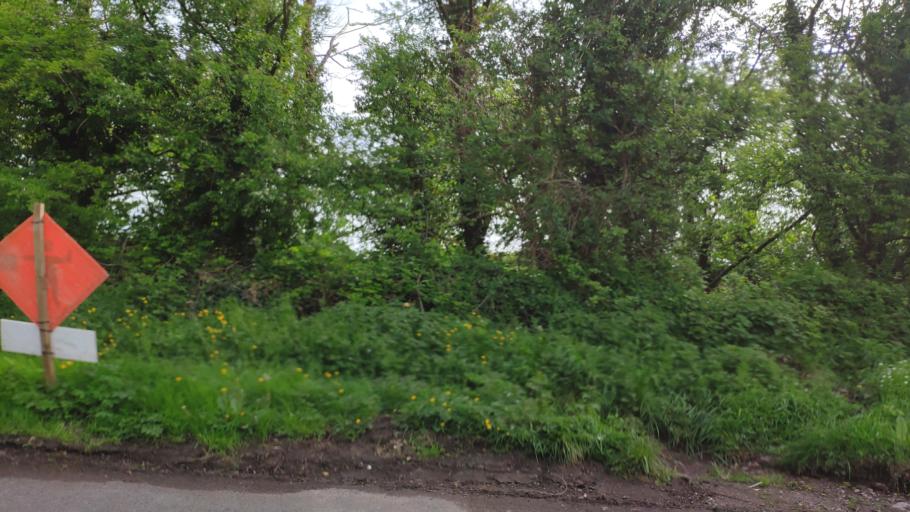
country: IE
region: Munster
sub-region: County Cork
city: Blarney
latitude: 51.9627
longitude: -8.5141
